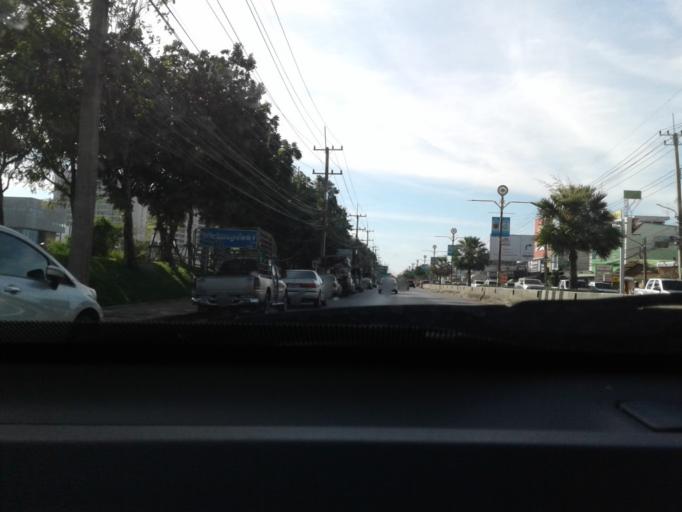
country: TH
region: Nakhon Pathom
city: Salaya
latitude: 13.8011
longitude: 100.3256
